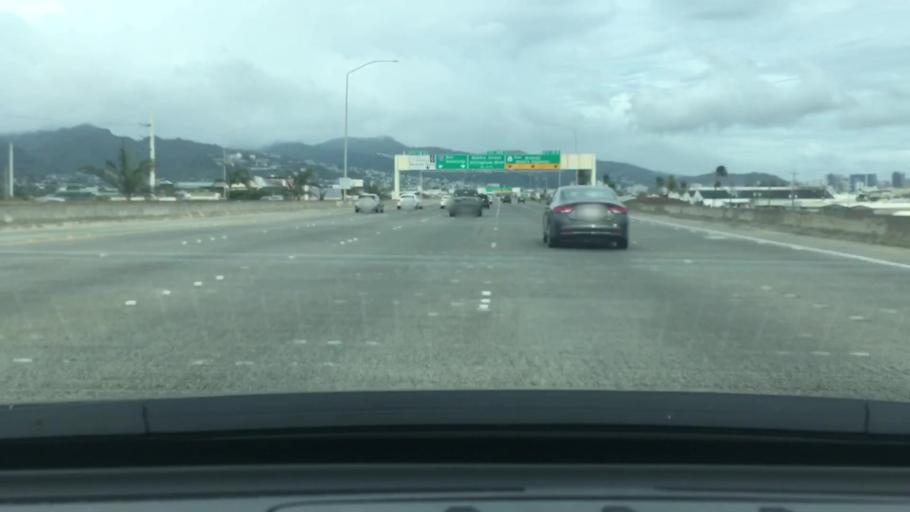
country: US
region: Hawaii
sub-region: Honolulu County
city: Halawa Heights
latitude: 21.3353
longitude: -157.9052
